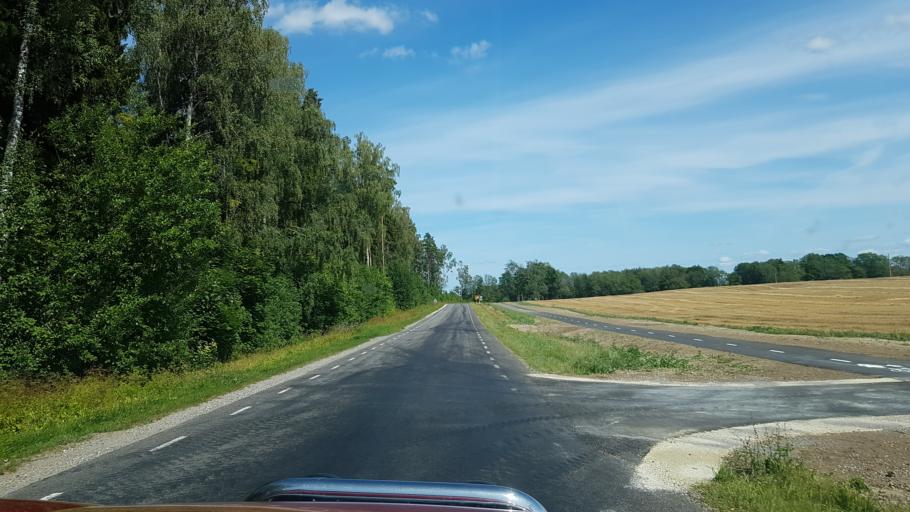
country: EE
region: Jaervamaa
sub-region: Jaerva-Jaani vald
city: Jarva-Jaani
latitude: 59.0395
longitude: 25.9377
